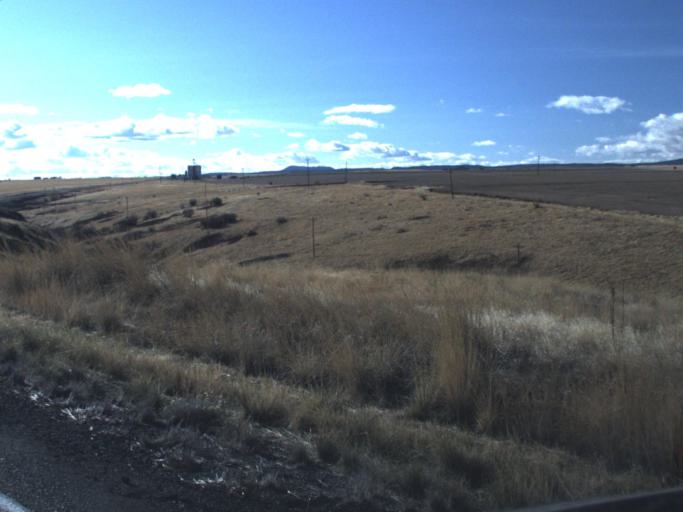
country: US
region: Washington
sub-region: Asotin County
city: Asotin
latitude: 46.2014
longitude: -117.0694
